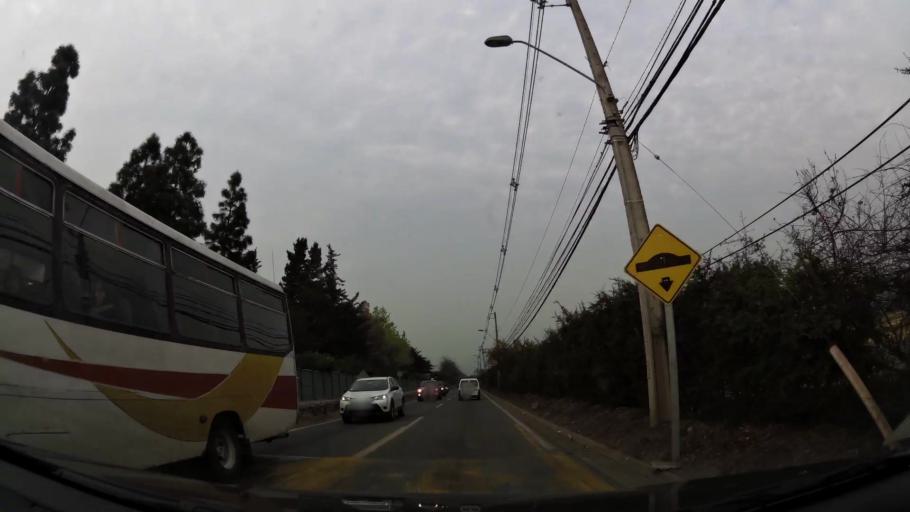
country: CL
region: Santiago Metropolitan
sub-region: Provincia de Chacabuco
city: Chicureo Abajo
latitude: -33.2863
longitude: -70.6601
